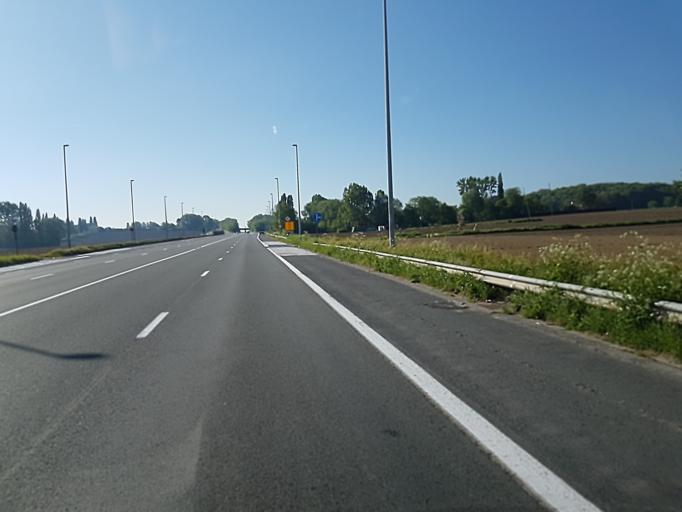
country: BE
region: Wallonia
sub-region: Province du Hainaut
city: Mouscron
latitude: 50.7660
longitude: 3.1941
